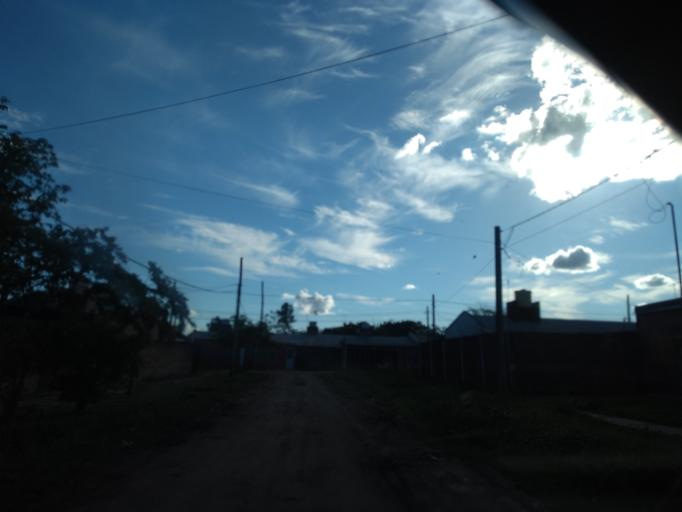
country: AR
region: Chaco
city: Fontana
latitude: -27.4131
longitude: -59.0421
